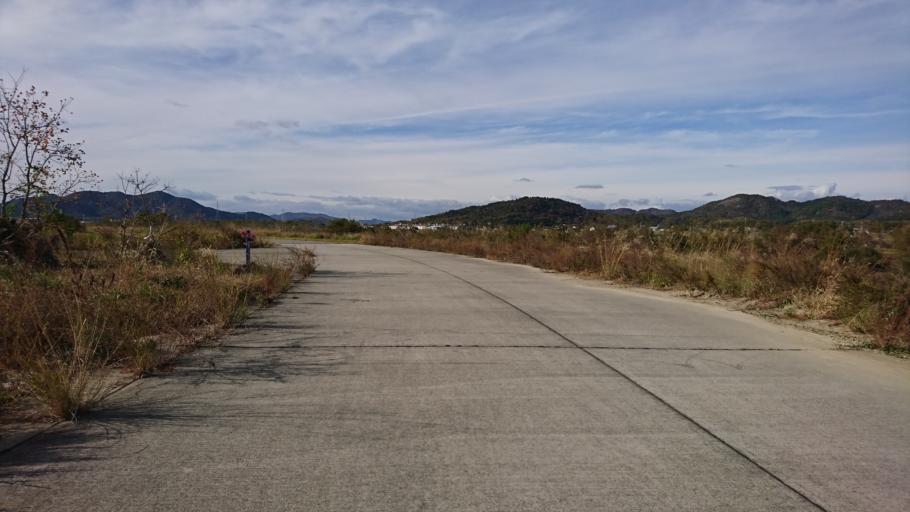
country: JP
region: Hyogo
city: Kakogawacho-honmachi
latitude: 34.7933
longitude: 134.8867
